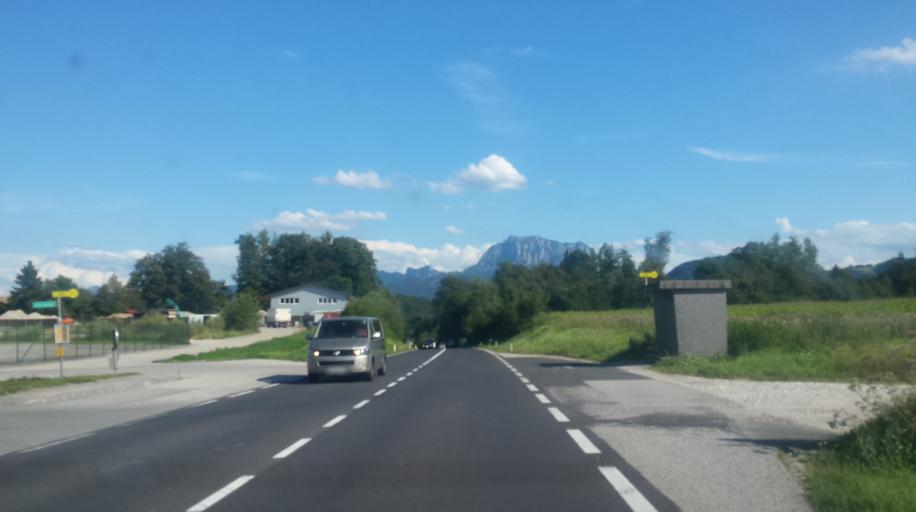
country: AT
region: Upper Austria
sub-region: Politischer Bezirk Gmunden
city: Altmunster
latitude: 47.9538
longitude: 13.7444
